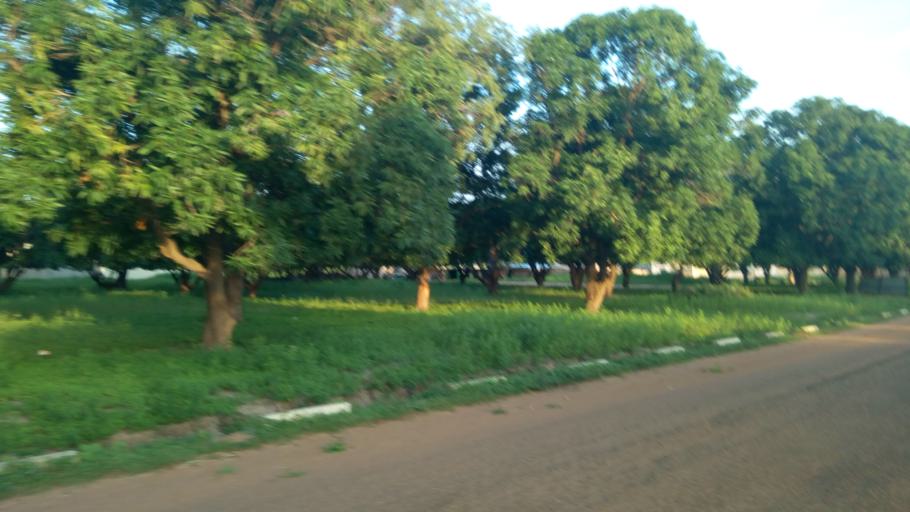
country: ML
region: Sikasso
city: Koutiala
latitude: 12.4059
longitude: -5.4449
